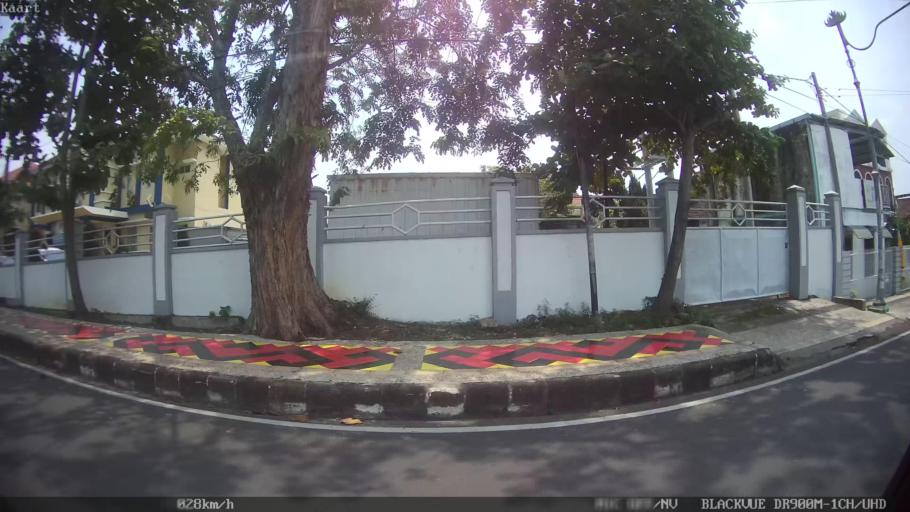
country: ID
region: Lampung
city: Bandarlampung
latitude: -5.4297
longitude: 105.2710
